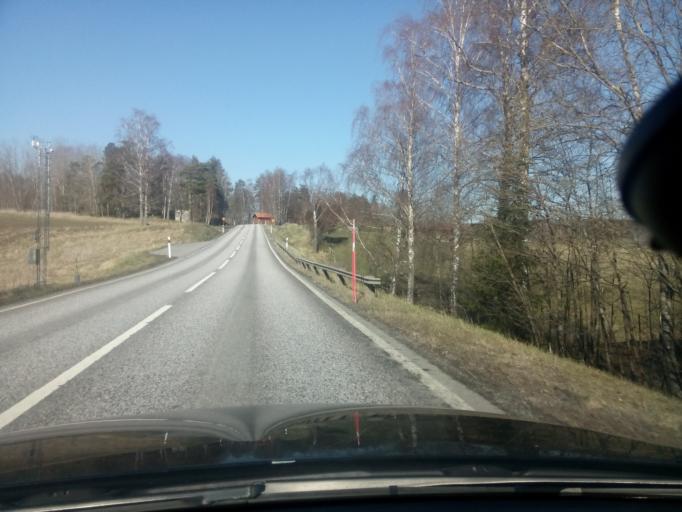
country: SE
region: Soedermanland
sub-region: Nykopings Kommun
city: Stigtomta
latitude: 58.9498
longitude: 16.8519
